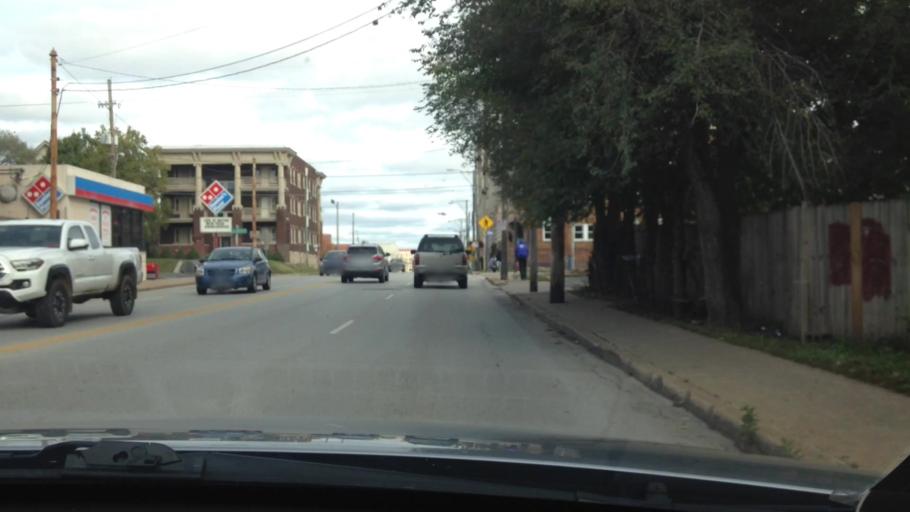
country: US
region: Kansas
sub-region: Johnson County
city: Westwood
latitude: 39.0567
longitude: -94.5893
